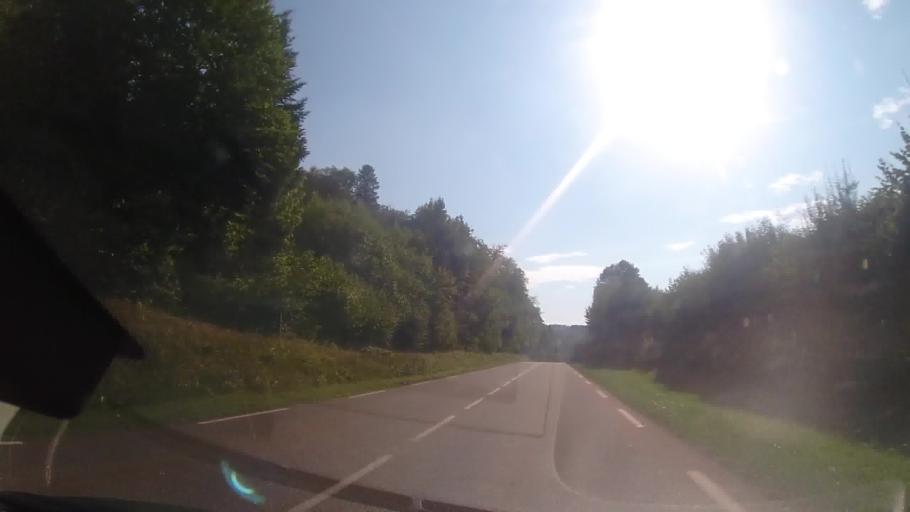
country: FR
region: Franche-Comte
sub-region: Departement du Jura
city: Clairvaux-les-Lacs
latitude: 46.5895
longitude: 5.8352
